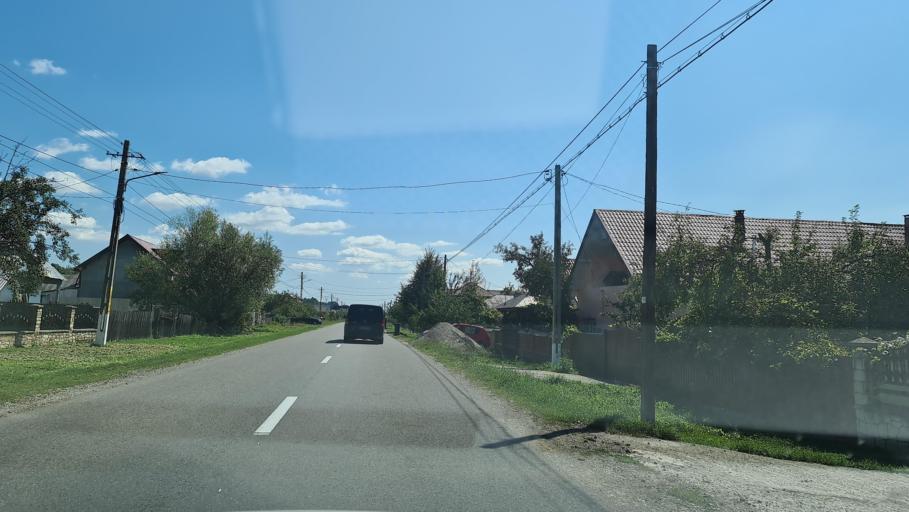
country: RO
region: Bacau
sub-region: Comuna Balcani
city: Balcani
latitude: 46.6416
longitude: 26.5712
